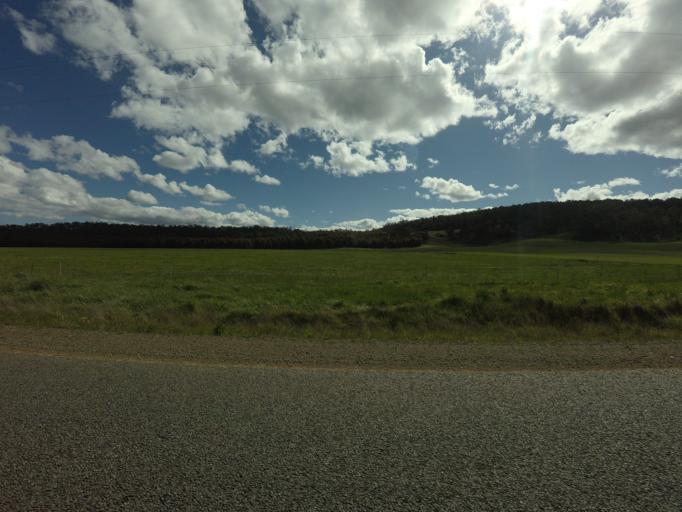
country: AU
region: Tasmania
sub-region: Brighton
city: Bridgewater
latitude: -42.4530
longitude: 147.3131
